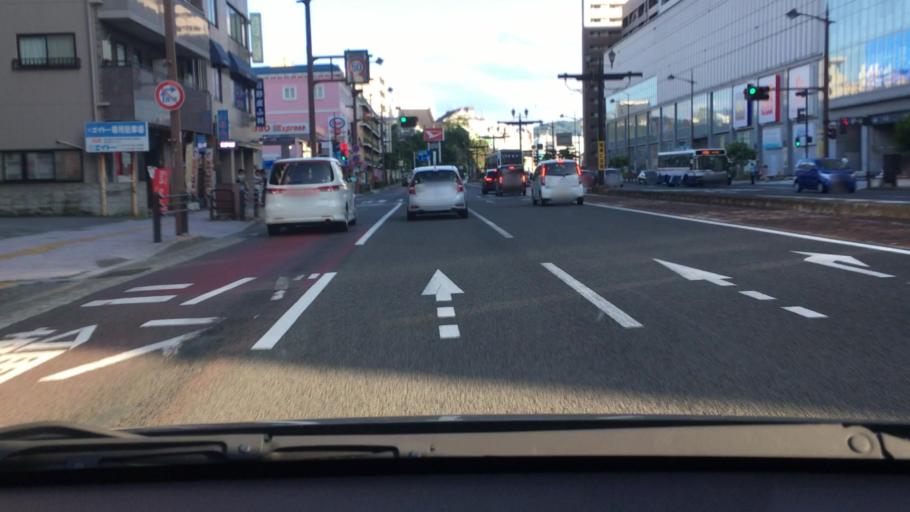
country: JP
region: Nagasaki
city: Nagasaki-shi
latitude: 32.7634
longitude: 129.8650
